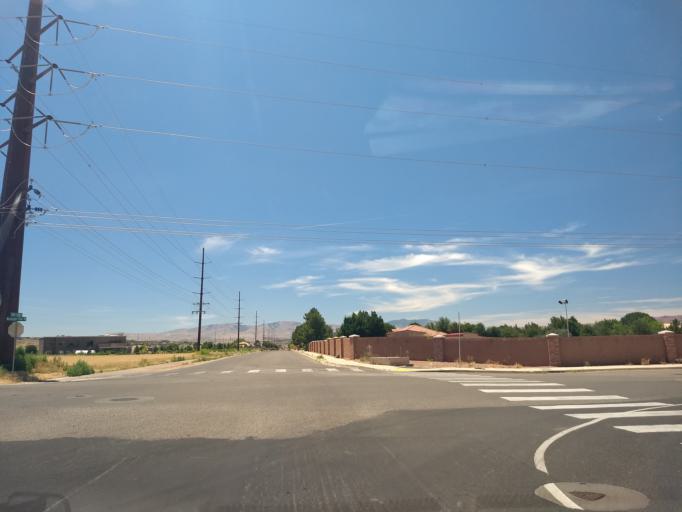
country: US
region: Utah
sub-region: Washington County
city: Washington
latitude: 37.0890
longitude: -113.4996
